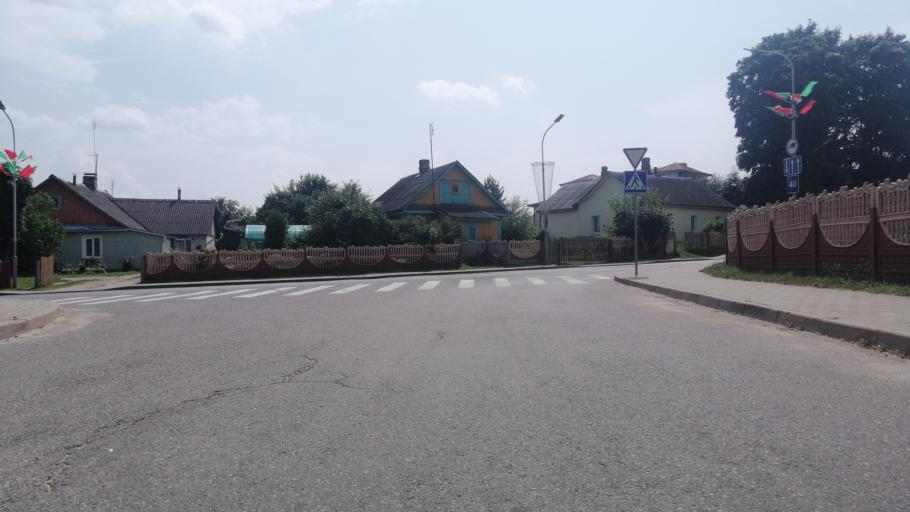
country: BY
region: Grodnenskaya
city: Navahrudak
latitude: 53.6000
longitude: 25.8344
